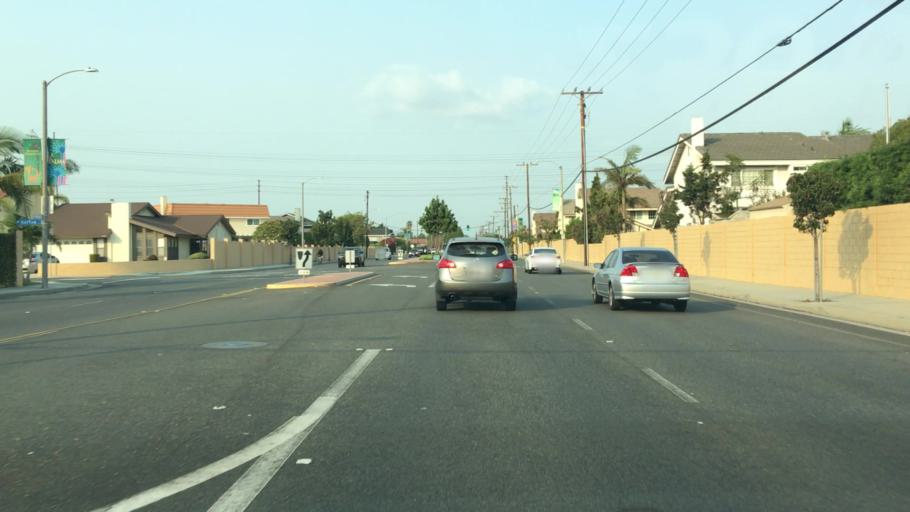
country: US
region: California
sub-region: Orange County
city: La Palma
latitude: 33.8476
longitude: -118.0460
